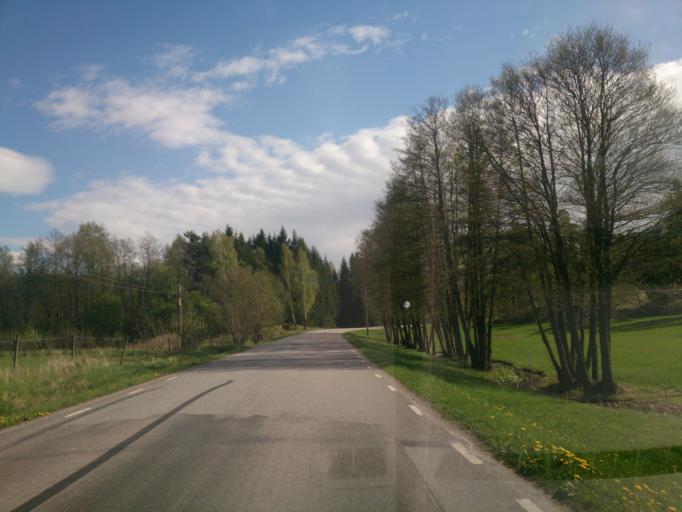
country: SE
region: OEstergoetland
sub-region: Linkopings Kommun
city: Ljungsbro
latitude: 58.5236
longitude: 15.5240
